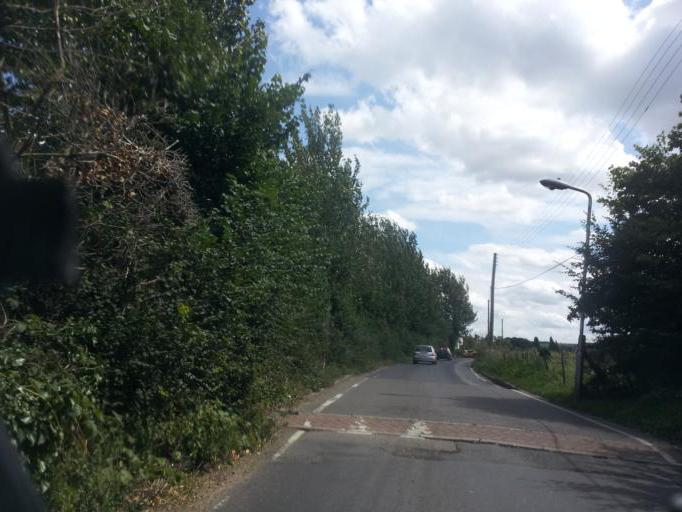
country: GB
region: England
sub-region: Kent
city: Newington
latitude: 51.3759
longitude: 0.6512
